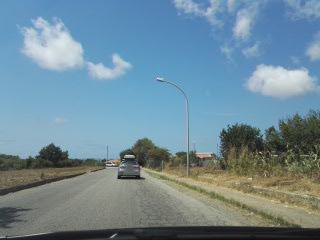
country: IT
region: Calabria
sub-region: Provincia di Vibo-Valentia
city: Ricadi
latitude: 38.6235
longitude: 15.8682
